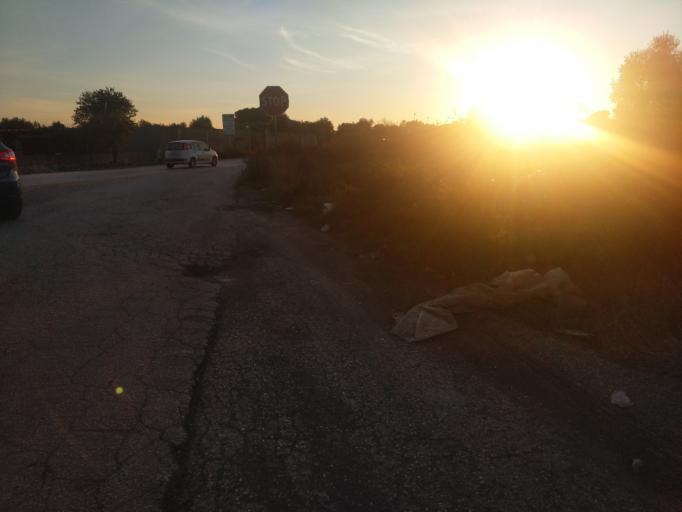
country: IT
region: Apulia
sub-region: Provincia di Bari
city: Modugno
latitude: 41.0861
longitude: 16.8022
